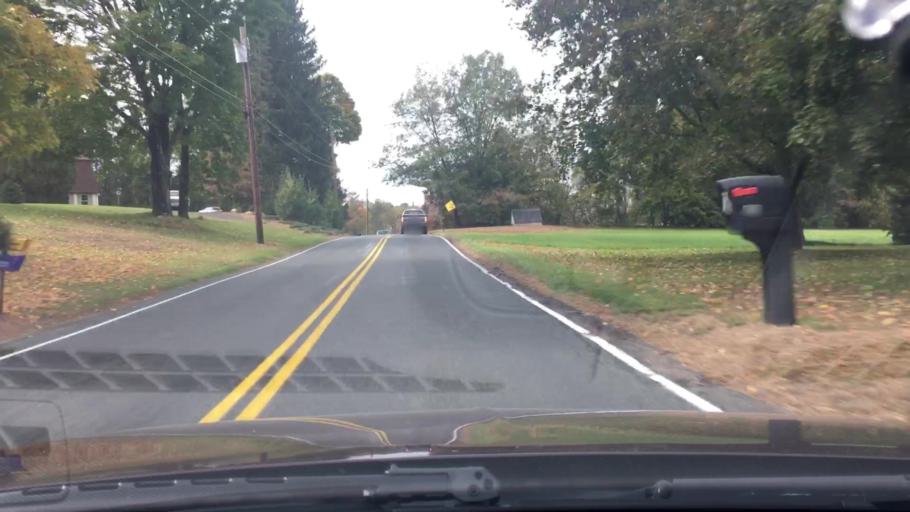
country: US
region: Connecticut
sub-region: Hartford County
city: Hazardville
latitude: 41.9966
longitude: -72.5001
